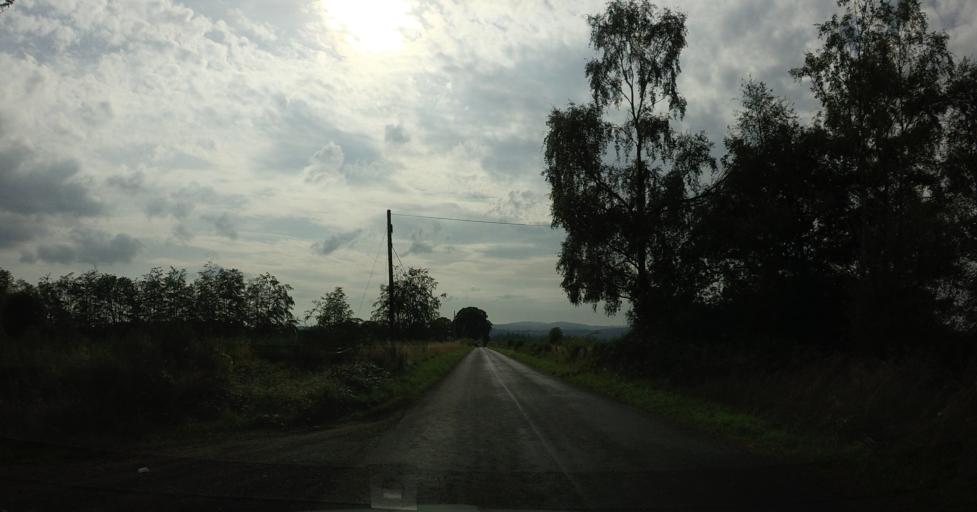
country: GB
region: Scotland
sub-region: Perth and Kinross
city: Auchterarder
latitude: 56.3505
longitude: -3.7300
